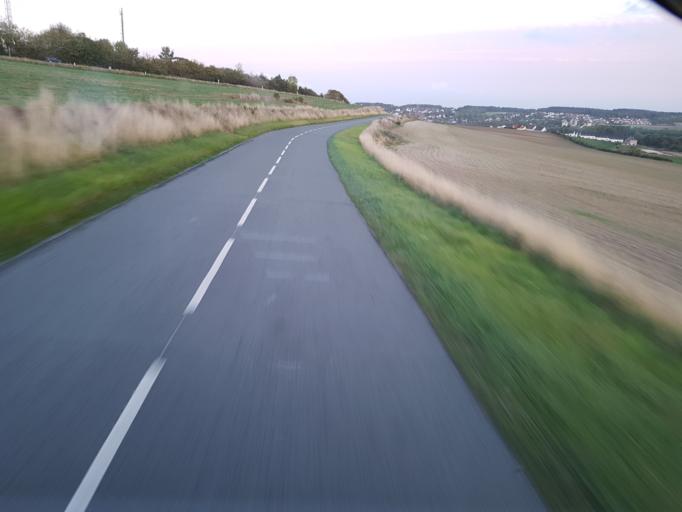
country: FR
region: Picardie
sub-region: Departement de la Somme
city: Ailly-sur-Noye
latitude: 49.7606
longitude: 2.3368
